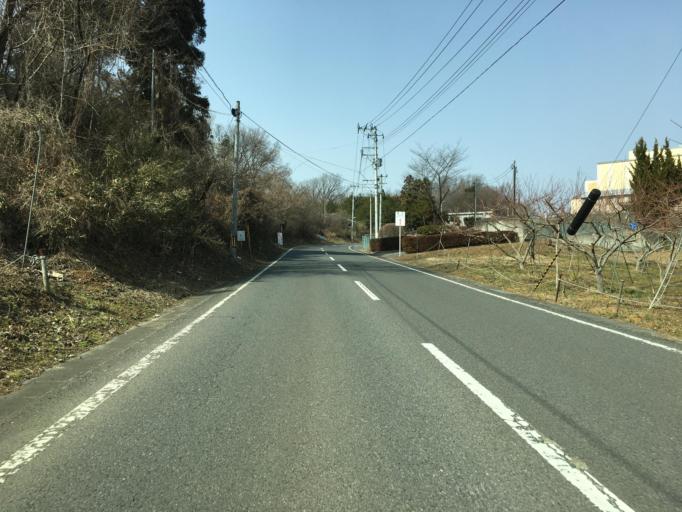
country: JP
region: Fukushima
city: Motomiya
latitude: 37.5295
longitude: 140.4115
